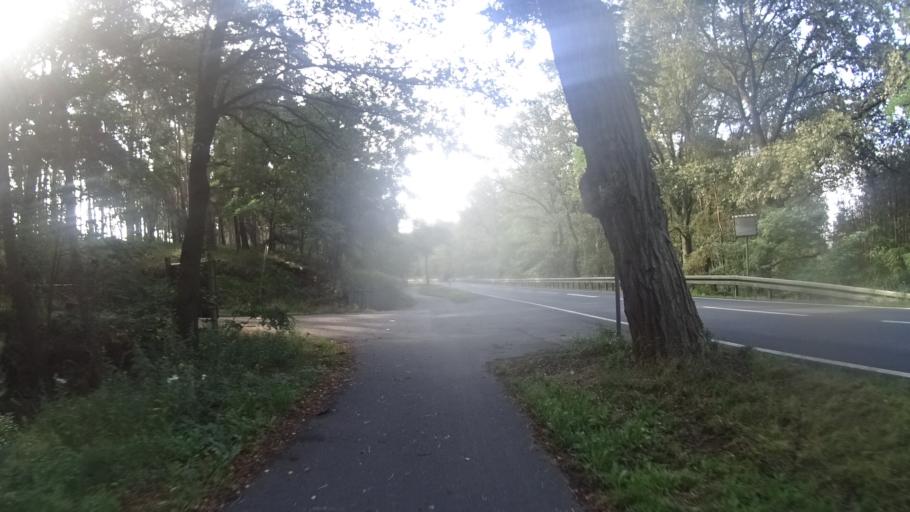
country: DE
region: Brandenburg
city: Wittenberge
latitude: 53.0129
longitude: 11.7073
